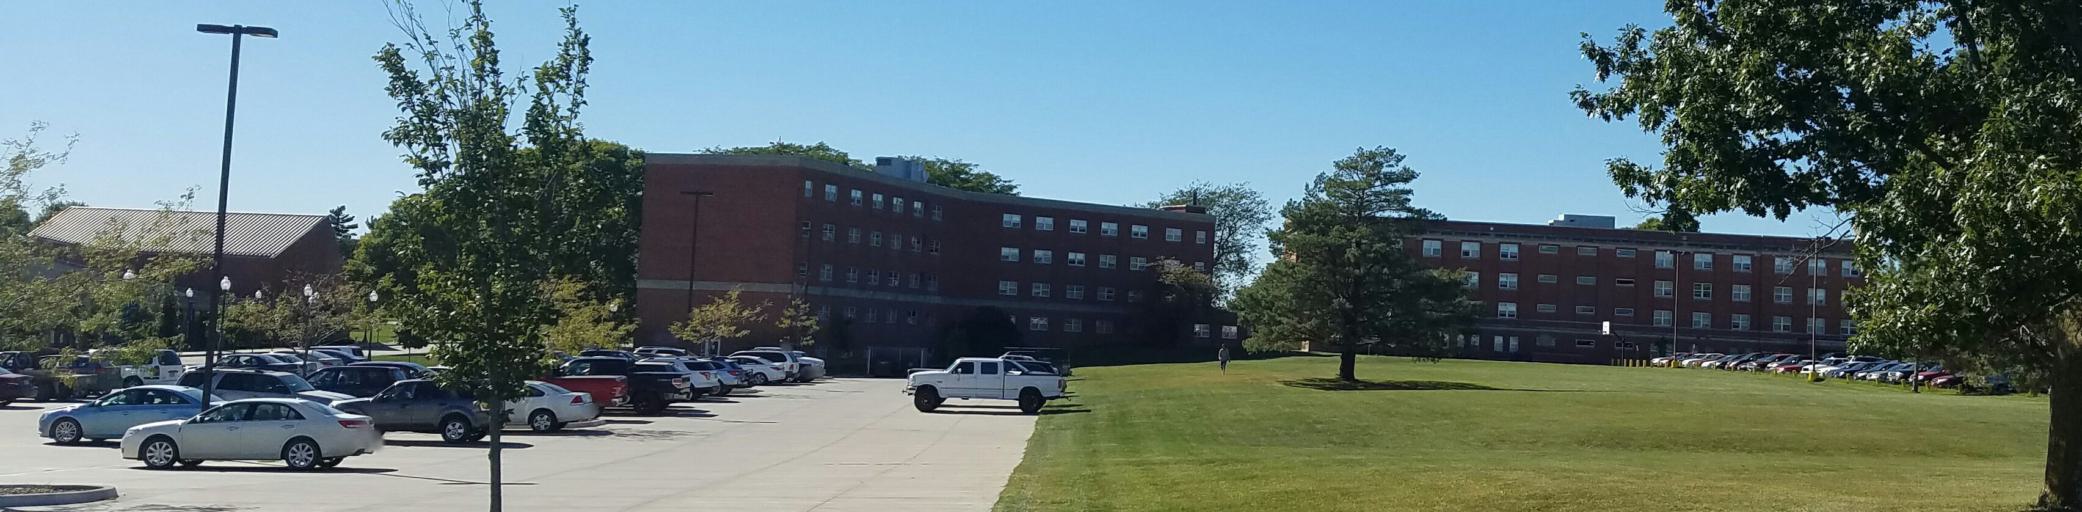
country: US
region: Iowa
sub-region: Decatur County
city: Lamoni
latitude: 40.6163
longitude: -93.9236
